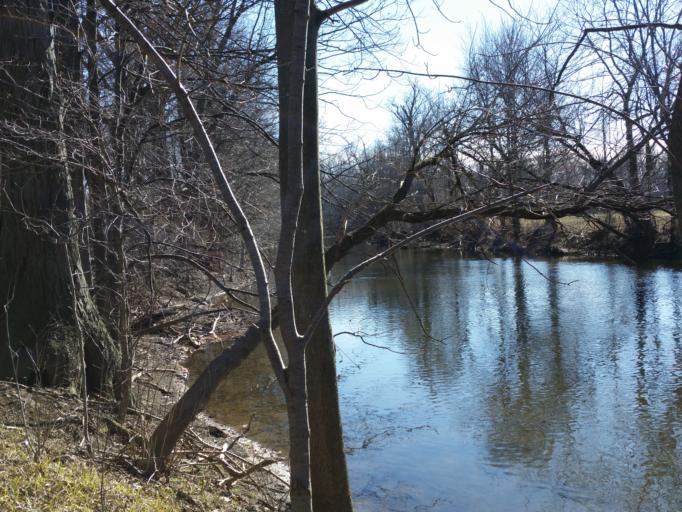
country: US
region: New York
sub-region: Monroe County
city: Churchville
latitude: 43.0869
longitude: -77.8043
